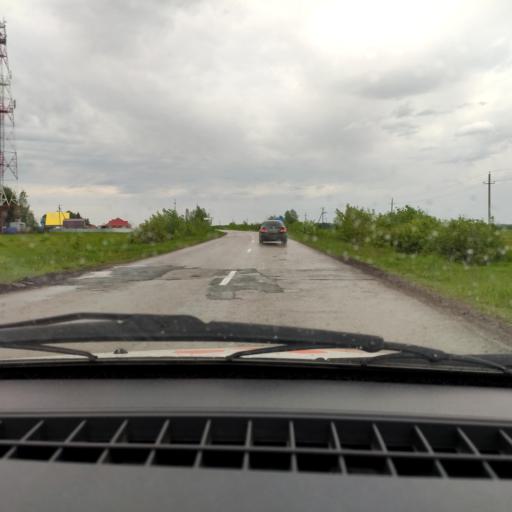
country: RU
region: Bashkortostan
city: Kudeyevskiy
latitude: 54.8420
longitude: 56.7954
